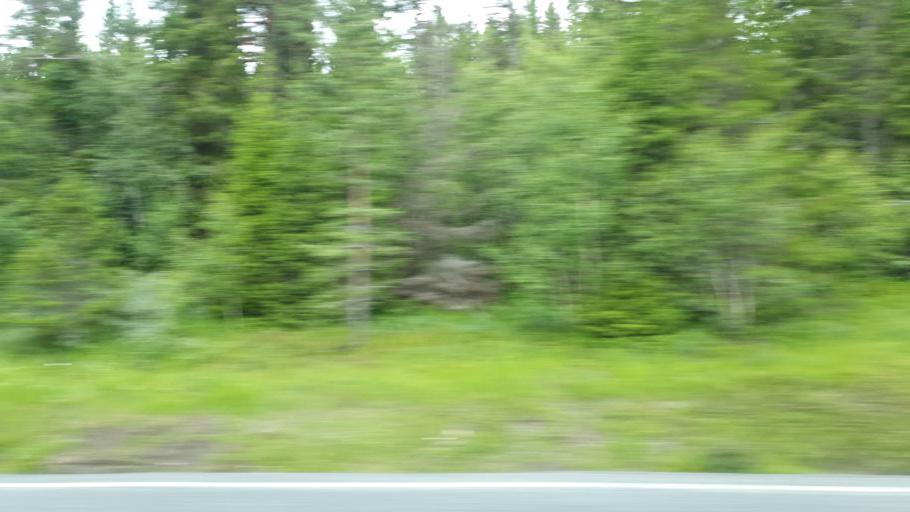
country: NO
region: Sor-Trondelag
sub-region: Rennebu
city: Berkak
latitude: 62.8465
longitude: 10.0174
